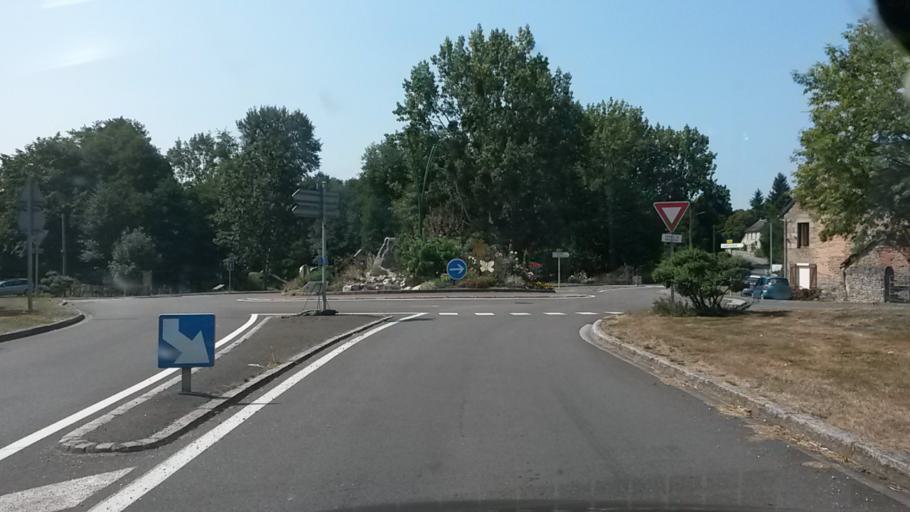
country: FR
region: Pays de la Loire
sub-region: Departement de la Mayenne
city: Saint-Pierre-des-Nids
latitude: 48.4026
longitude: -0.0888
